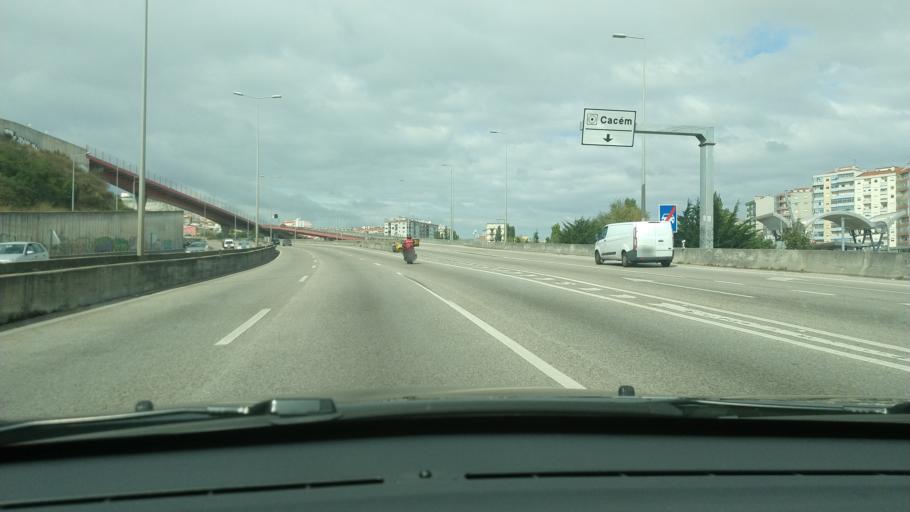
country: PT
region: Lisbon
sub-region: Sintra
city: Cacem
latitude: 38.7642
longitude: -9.2980
